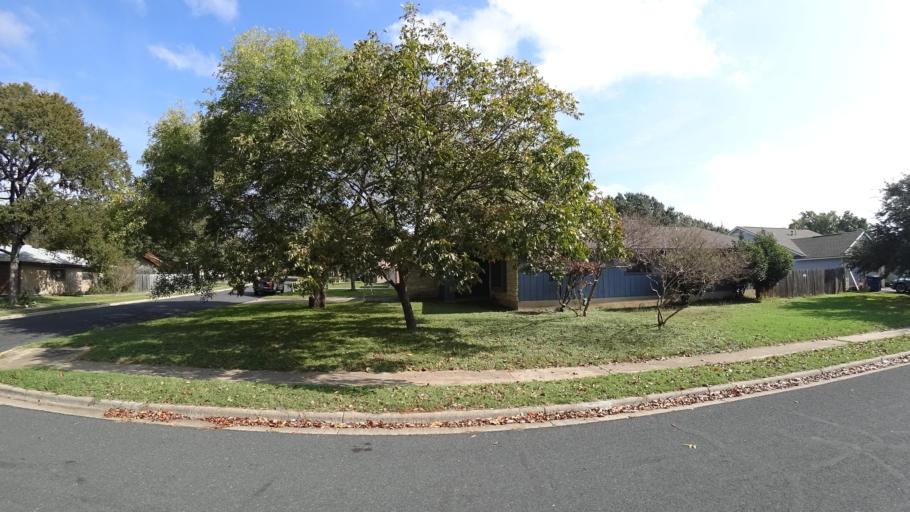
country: US
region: Texas
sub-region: Travis County
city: Wells Branch
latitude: 30.4279
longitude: -97.7255
